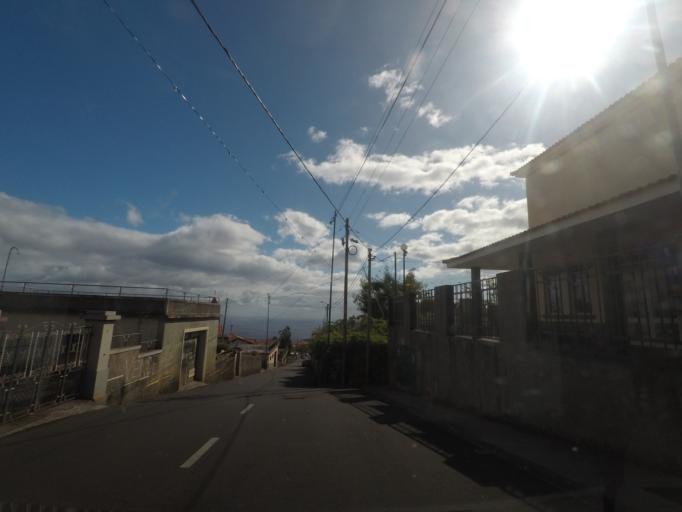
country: PT
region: Madeira
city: Camara de Lobos
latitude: 32.6745
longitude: -16.9492
